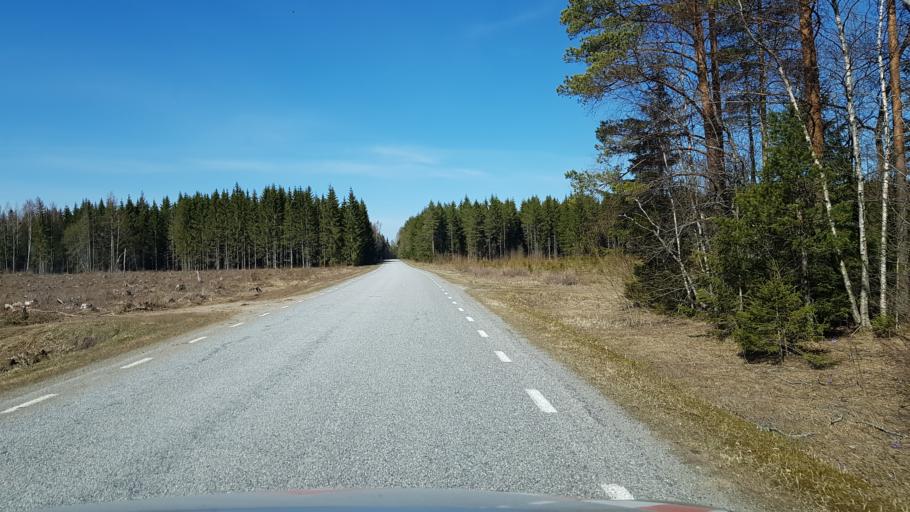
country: EE
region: Laeaene-Virumaa
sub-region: Vinni vald
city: Vinni
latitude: 59.1735
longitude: 26.5057
